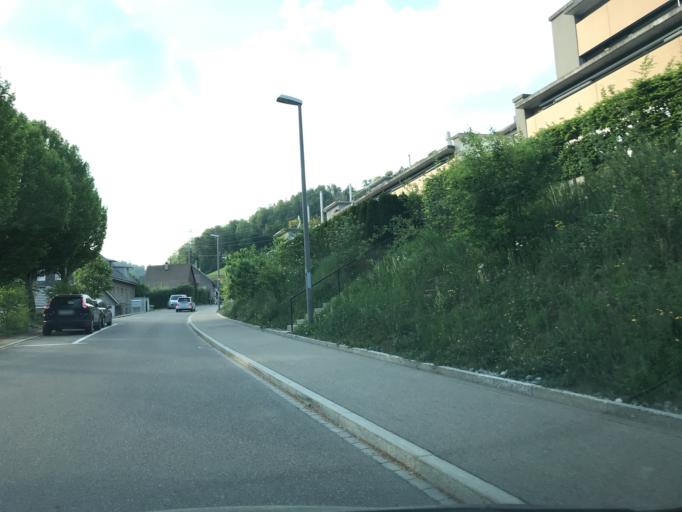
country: CH
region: Zurich
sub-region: Bezirk Winterthur
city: Toess (Kreis 4) / Vorder-Daettnau
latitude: 47.4832
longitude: 8.6948
